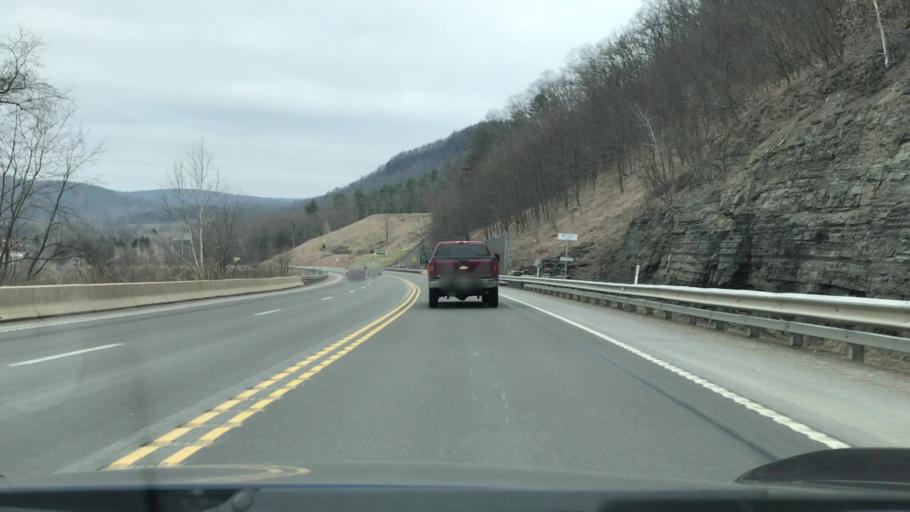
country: US
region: Pennsylvania
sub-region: Bradford County
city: Towanda
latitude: 41.7690
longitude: -76.3691
